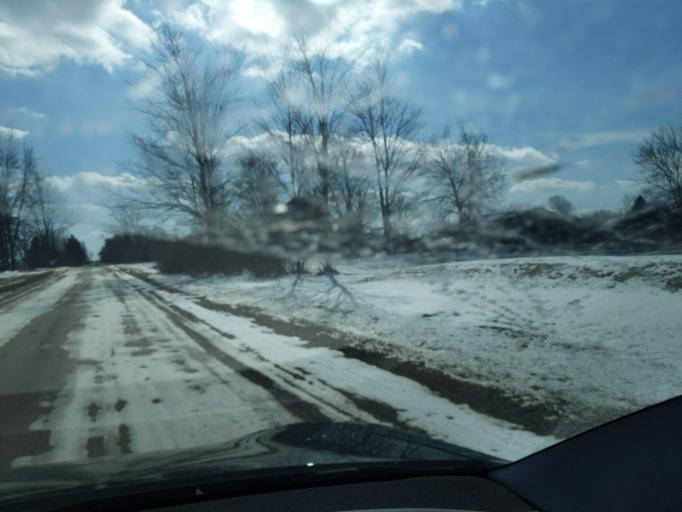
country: US
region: Michigan
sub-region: Livingston County
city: Fowlerville
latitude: 42.6169
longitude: -84.0910
